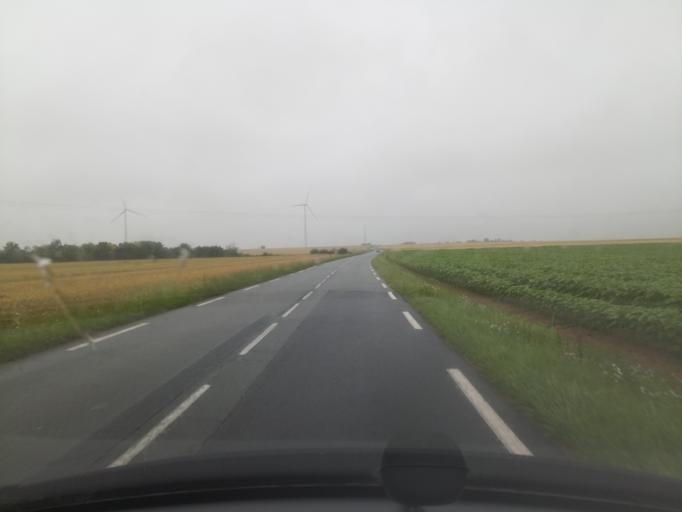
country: FR
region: Poitou-Charentes
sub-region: Departement de la Charente-Maritime
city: Saint-Jean-de-Liversay
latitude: 46.2485
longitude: -0.8814
